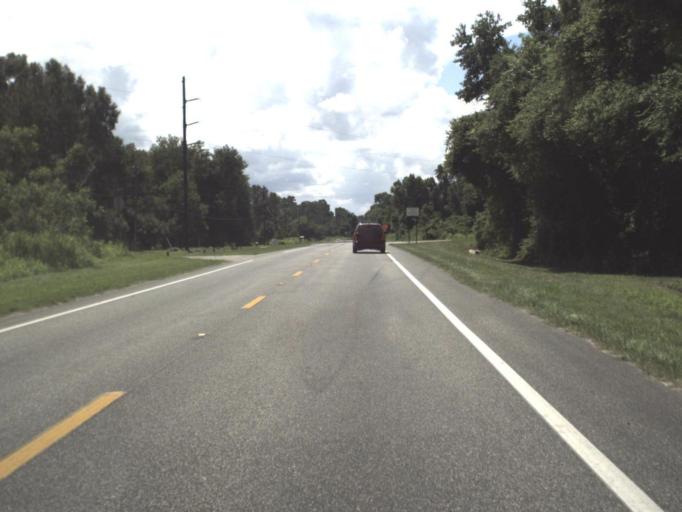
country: US
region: Florida
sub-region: Putnam County
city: Crescent City
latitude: 29.4565
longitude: -81.5182
